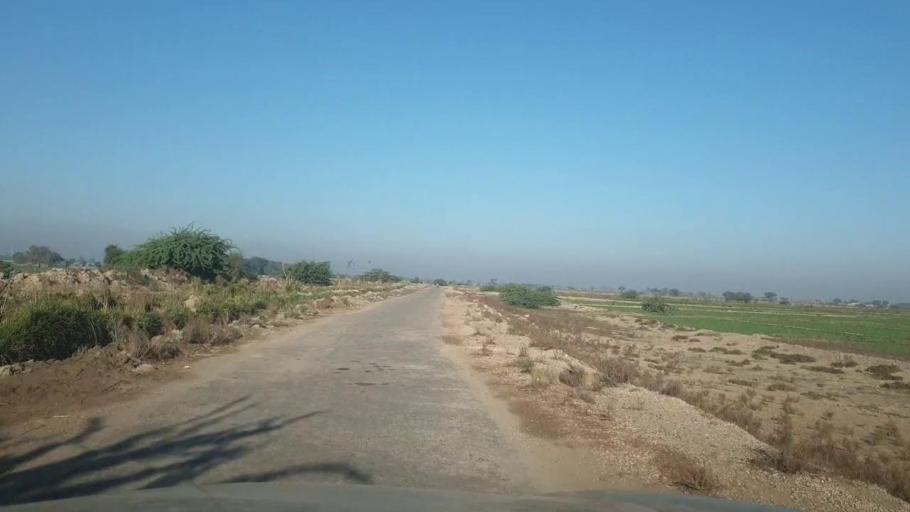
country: PK
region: Sindh
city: Bhan
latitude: 26.5510
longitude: 67.6986
